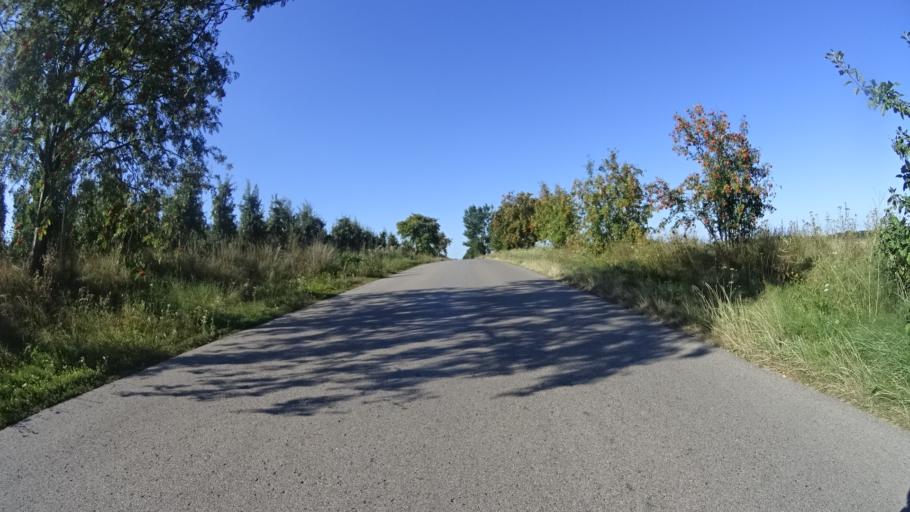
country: PL
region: Masovian Voivodeship
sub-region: Powiat bialobrzeski
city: Wysmierzyce
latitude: 51.6627
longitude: 20.8310
